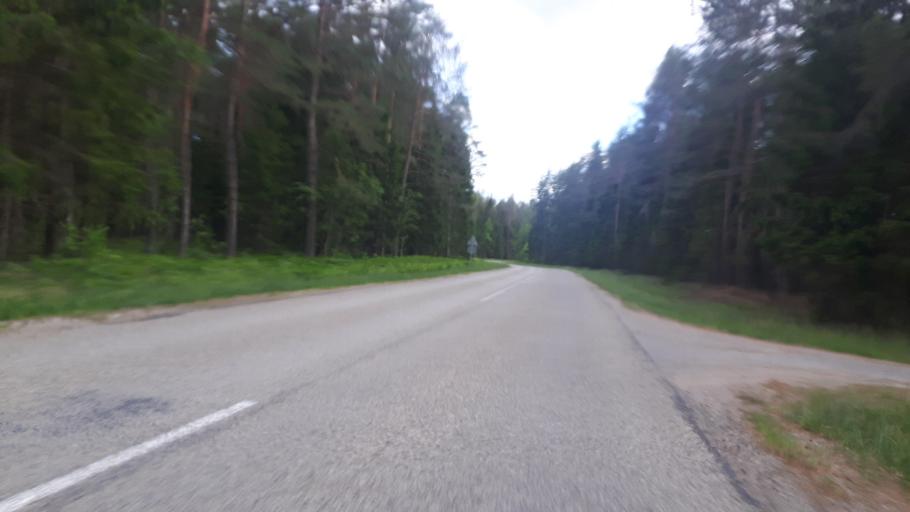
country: LV
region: Engure
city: Smarde
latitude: 57.0149
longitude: 23.3427
